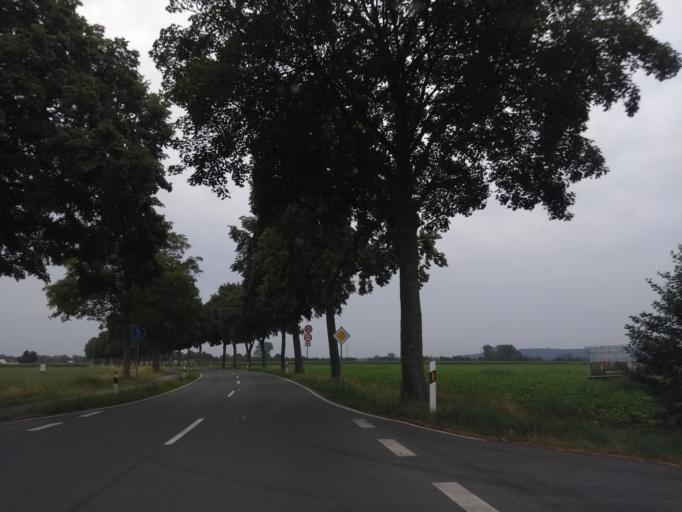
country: DE
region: North Rhine-Westphalia
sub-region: Regierungsbezirk Dusseldorf
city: Kleve
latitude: 51.8274
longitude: 6.1030
